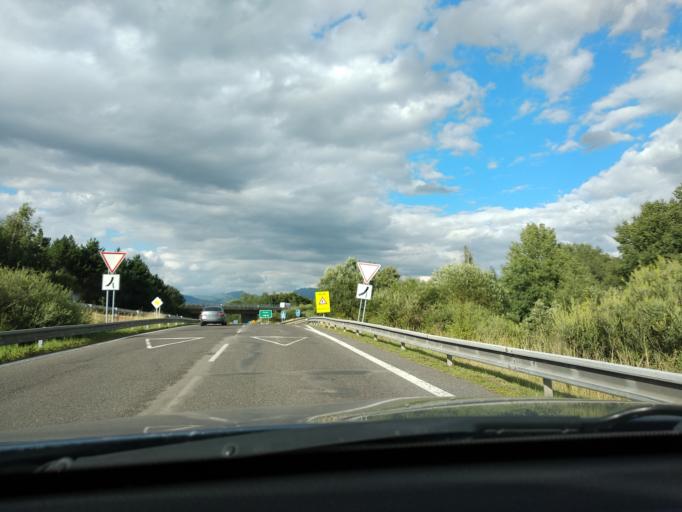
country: SK
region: Zilinsky
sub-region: Okres Zilina
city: Liptovsky Hradok
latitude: 49.0583
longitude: 19.7451
